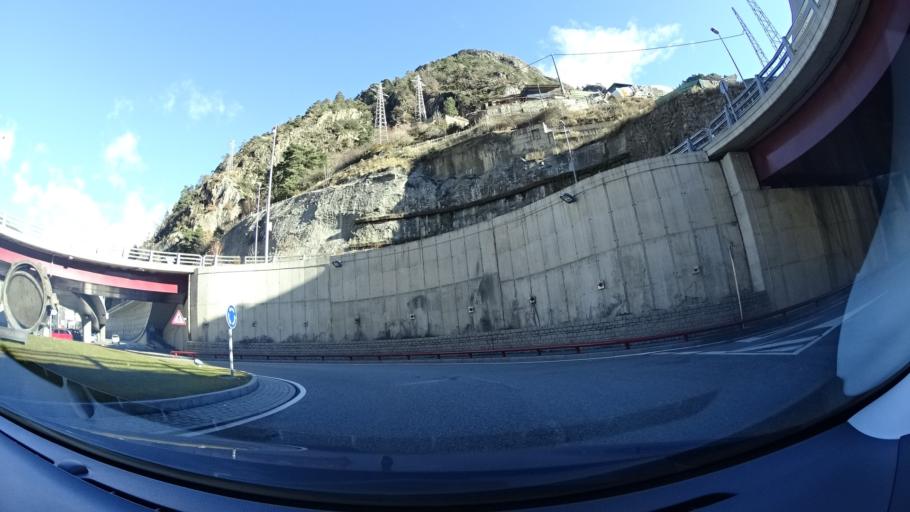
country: AD
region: Escaldes-Engordany
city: les Escaldes
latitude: 42.5157
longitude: 1.5572
